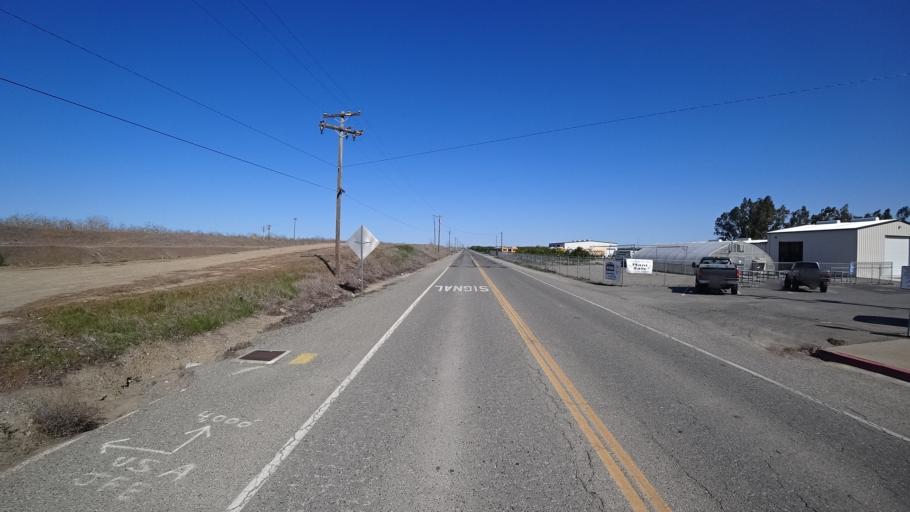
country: US
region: California
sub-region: Glenn County
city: Hamilton City
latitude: 39.7461
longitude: -122.0202
